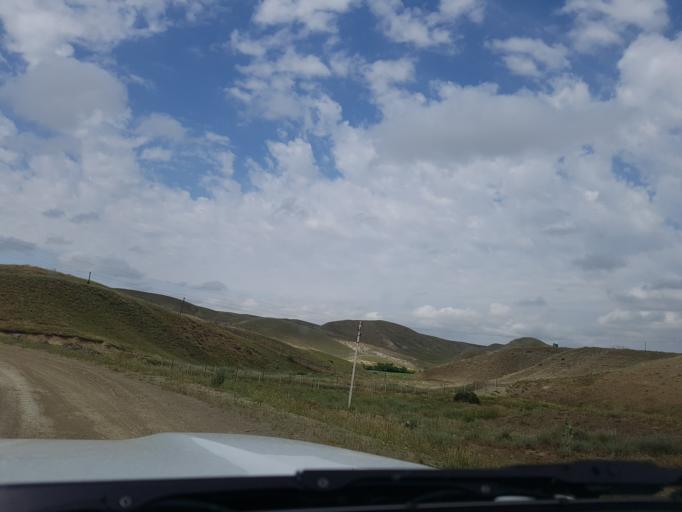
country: TM
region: Balkan
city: Magtymguly
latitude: 38.2638
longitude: 56.7901
